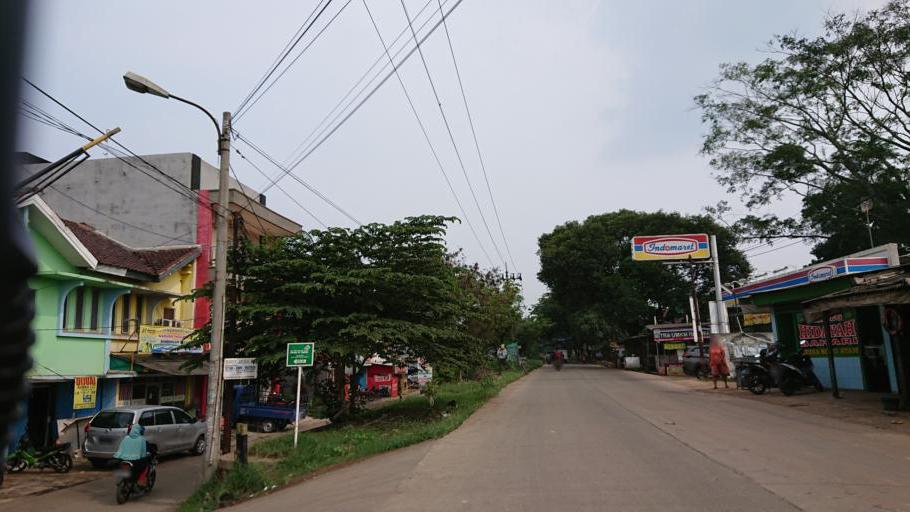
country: ID
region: West Java
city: Parung
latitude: -6.3863
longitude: 106.6813
